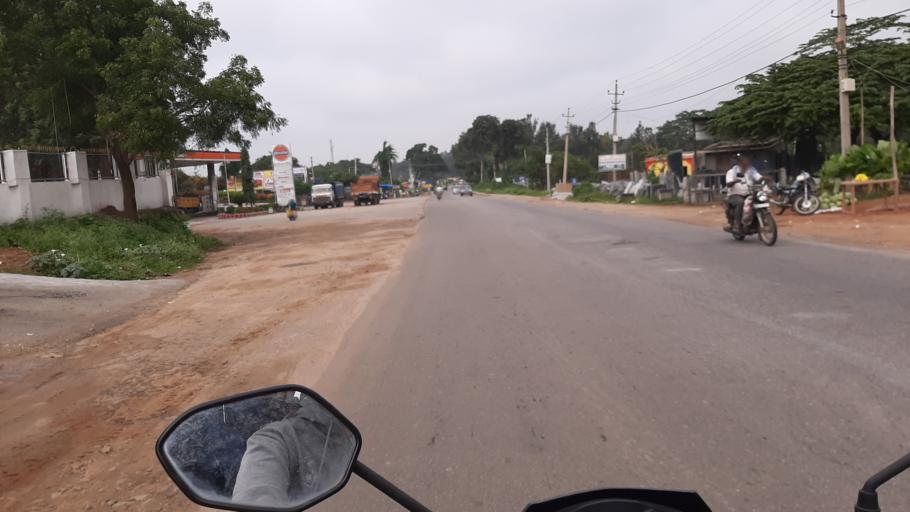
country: IN
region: Karnataka
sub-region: Bangalore Rural
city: Nelamangala
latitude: 12.9719
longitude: 77.4166
